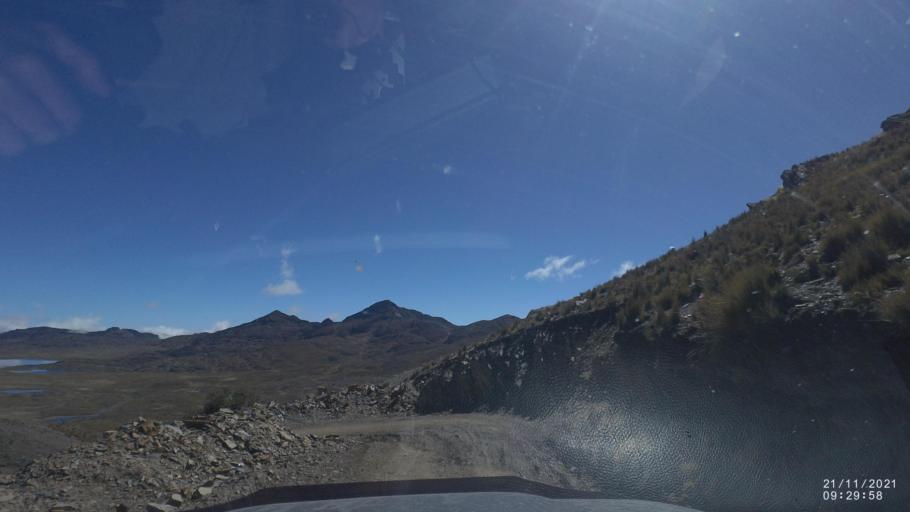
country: BO
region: Cochabamba
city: Cochabamba
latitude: -17.0766
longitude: -66.2573
